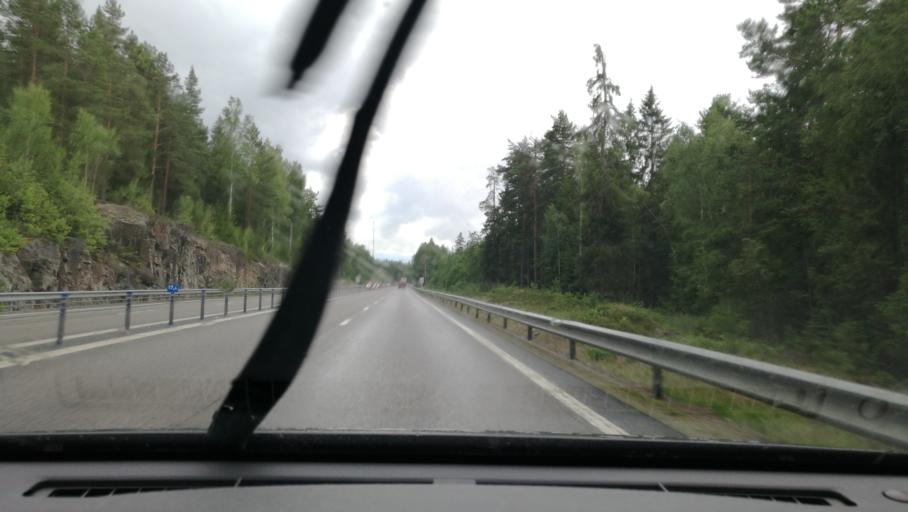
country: SE
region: OEstergoetland
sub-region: Norrkopings Kommun
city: Jursla
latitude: 58.8042
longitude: 16.1522
